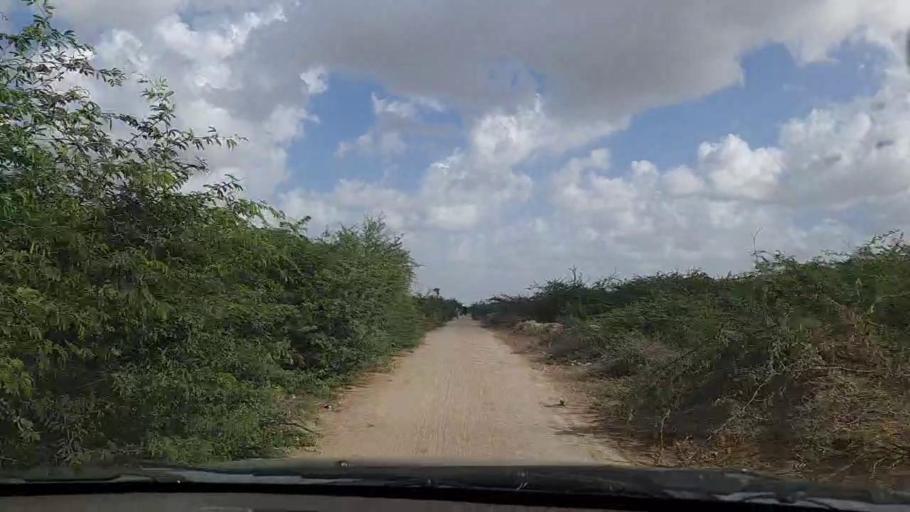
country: PK
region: Sindh
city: Keti Bandar
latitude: 24.0886
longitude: 67.6146
